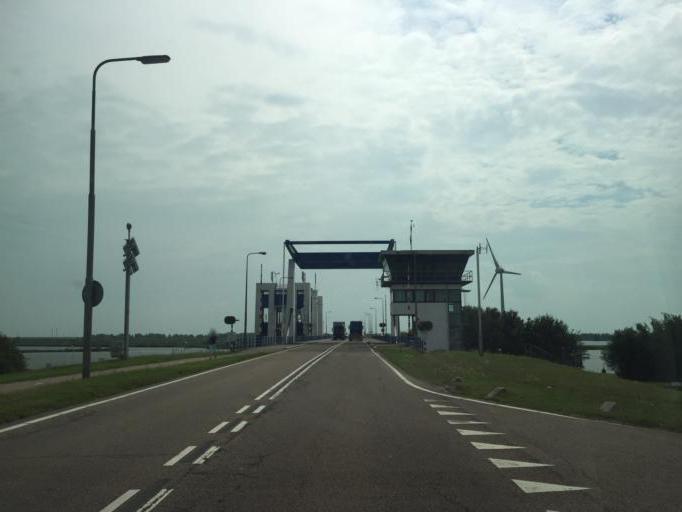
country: NL
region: North Holland
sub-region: Gemeente Enkhuizen
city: Enkhuizen
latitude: 52.6930
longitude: 5.2821
